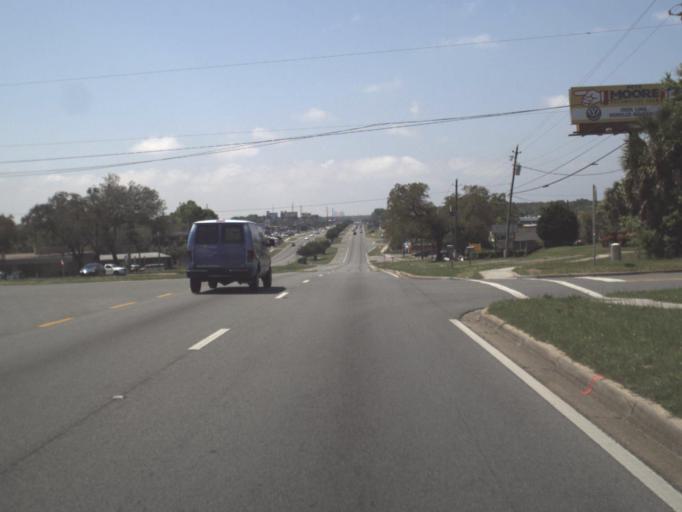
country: US
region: Florida
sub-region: Escambia County
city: West Pensacola
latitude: 30.4143
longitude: -87.2762
